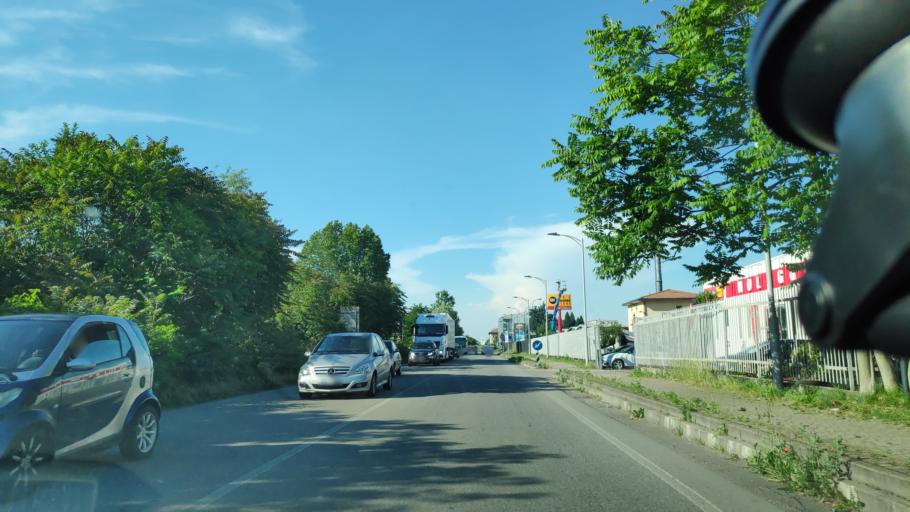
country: IT
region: Lombardy
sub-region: Citta metropolitana di Milano
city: Rozzano
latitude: 45.3842
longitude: 9.1455
